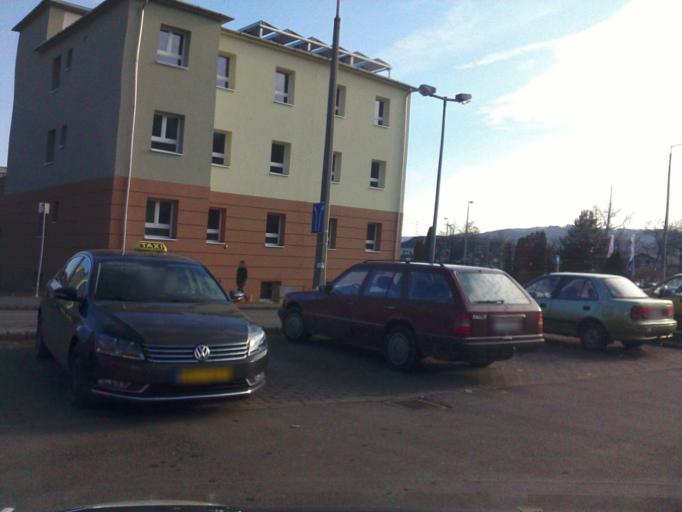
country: HU
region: Nograd
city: Salgotarjan
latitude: 48.1047
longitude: 19.8021
